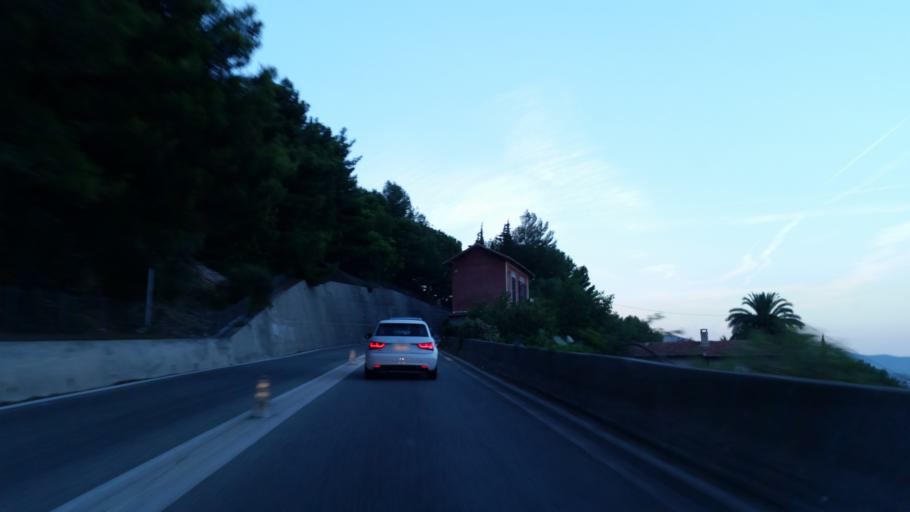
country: MC
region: Commune de Monaco
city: Saint-Roman
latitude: 43.7589
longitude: 7.4441
